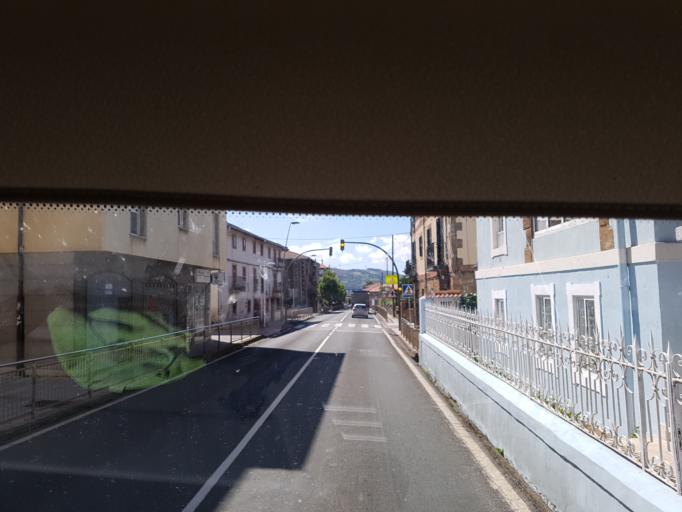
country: ES
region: Basque Country
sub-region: Bizkaia
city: San Julian de Muskiz
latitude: 43.3183
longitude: -3.0950
